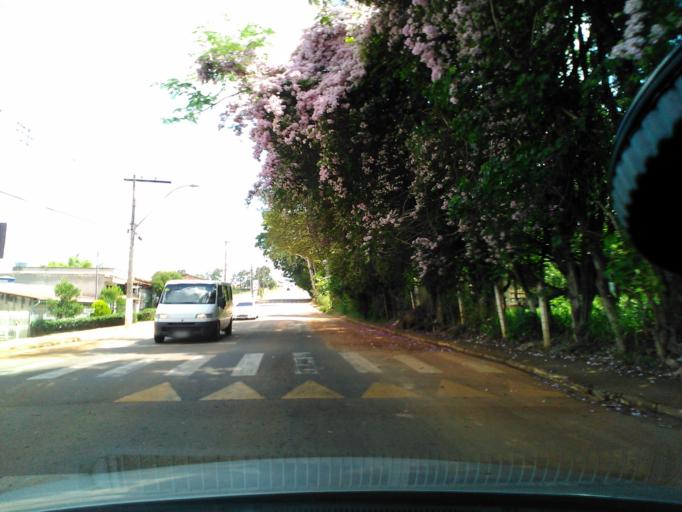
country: BR
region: Minas Gerais
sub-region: Tres Coracoes
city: Tres Coracoes
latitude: -21.7257
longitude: -45.2630
